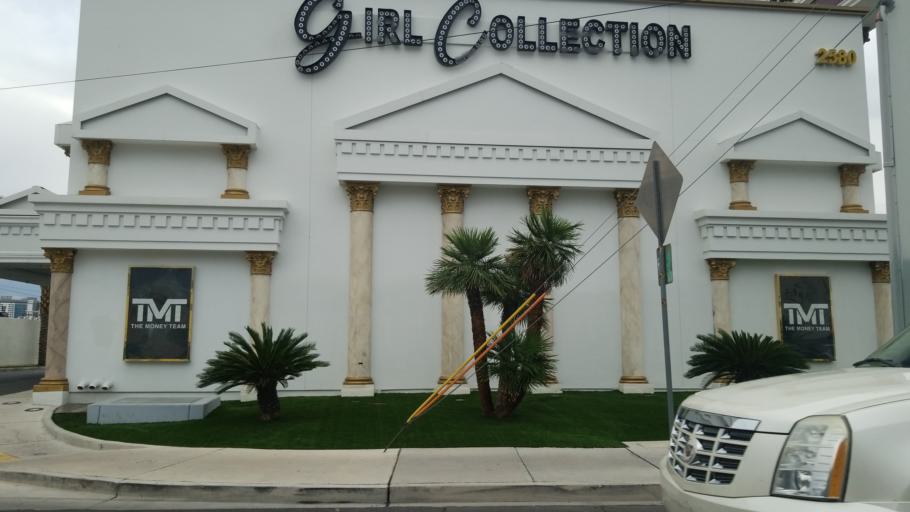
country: US
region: Nevada
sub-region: Clark County
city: Las Vegas
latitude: 36.1427
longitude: -115.1694
